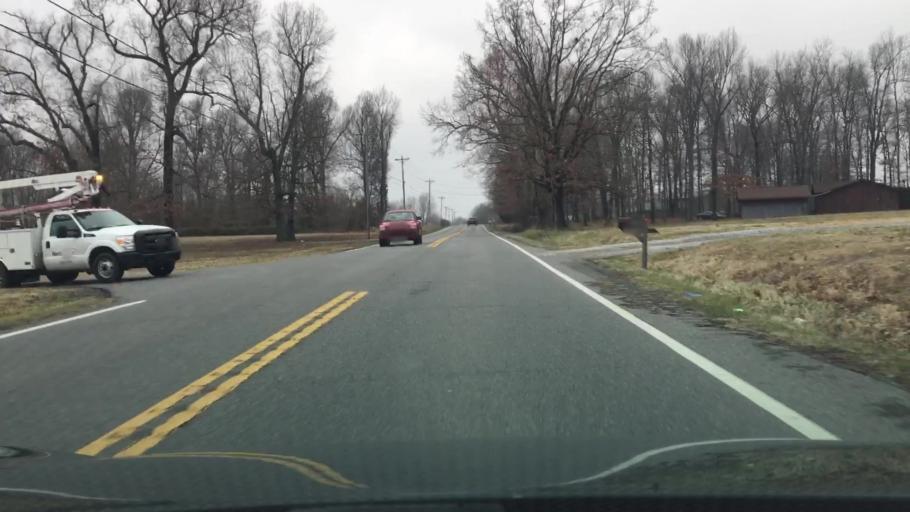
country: US
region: Kentucky
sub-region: Marshall County
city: Calvert City
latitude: 36.9505
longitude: -88.3685
